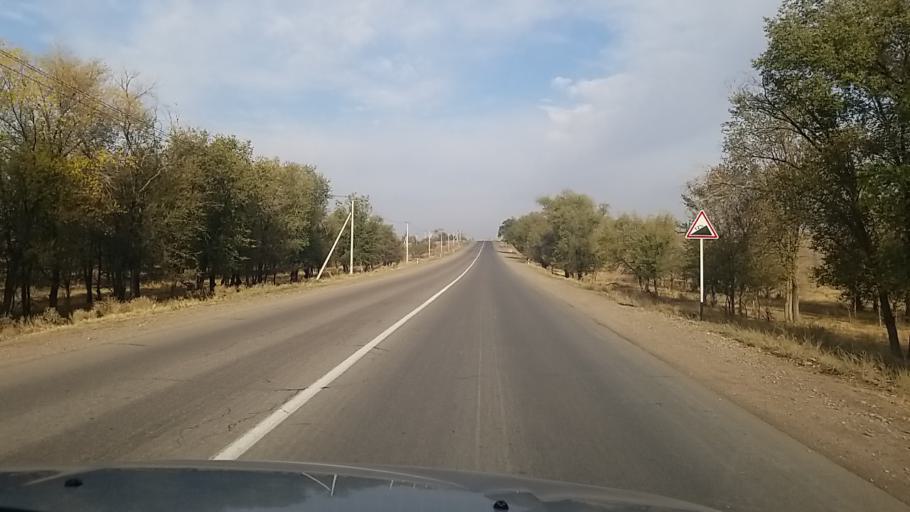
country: KZ
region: Almaty Oblysy
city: Burunday
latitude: 43.4713
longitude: 76.6974
